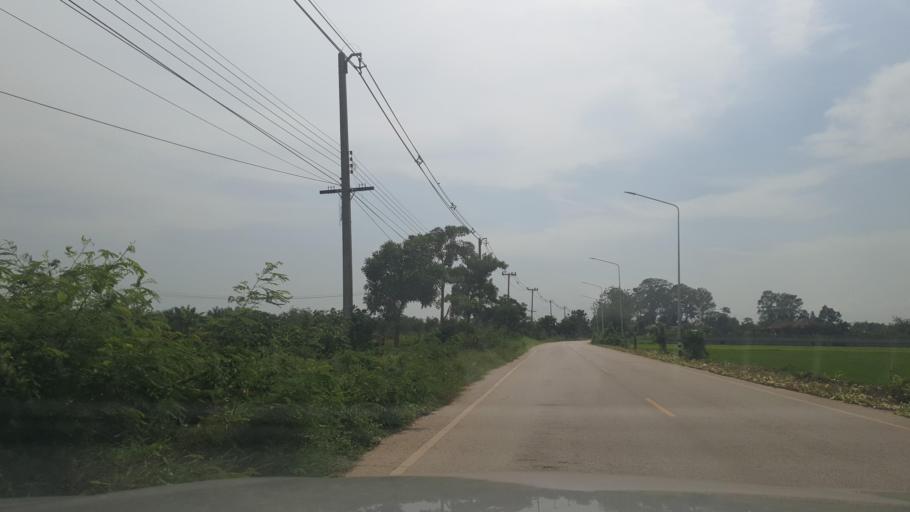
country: TH
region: Sukhothai
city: Si Samrong
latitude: 17.1405
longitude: 99.8362
